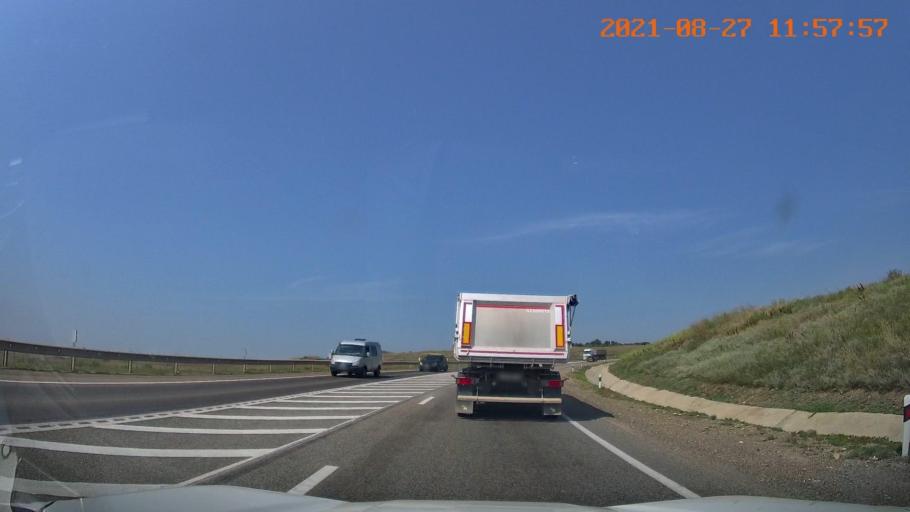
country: RU
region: Stavropol'skiy
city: Tatarka
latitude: 44.9290
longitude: 41.9133
